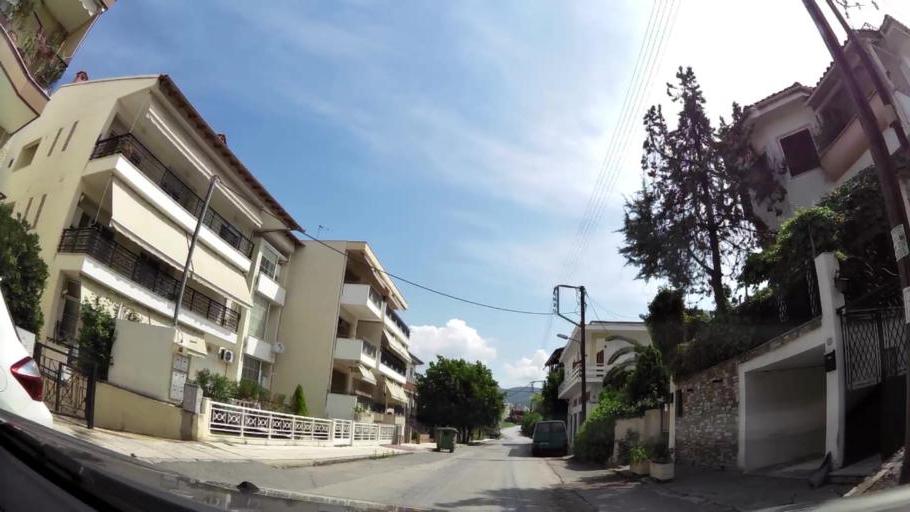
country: GR
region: Central Macedonia
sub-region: Nomos Thessalonikis
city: Pylaia
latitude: 40.6023
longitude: 22.9924
